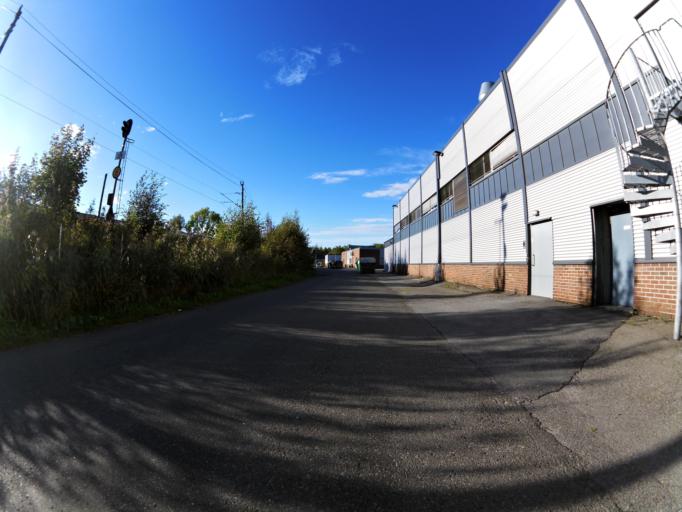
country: NO
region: Ostfold
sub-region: Sarpsborg
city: Sarpsborg
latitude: 59.2677
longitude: 11.0319
